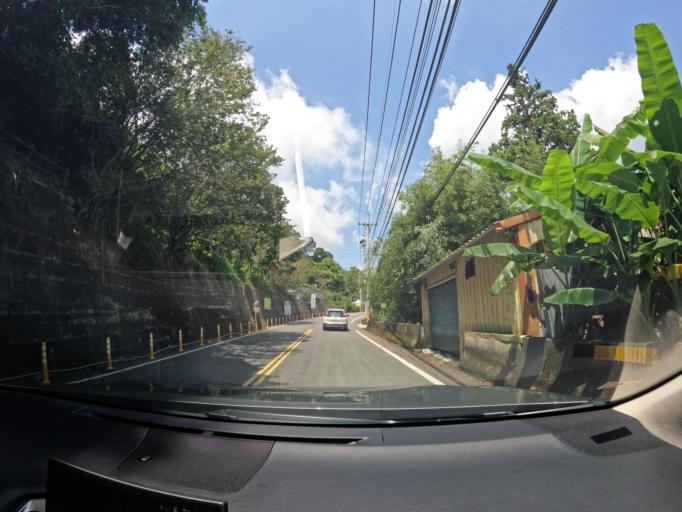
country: TW
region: Taiwan
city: Fengyuan
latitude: 24.3855
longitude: 120.8228
